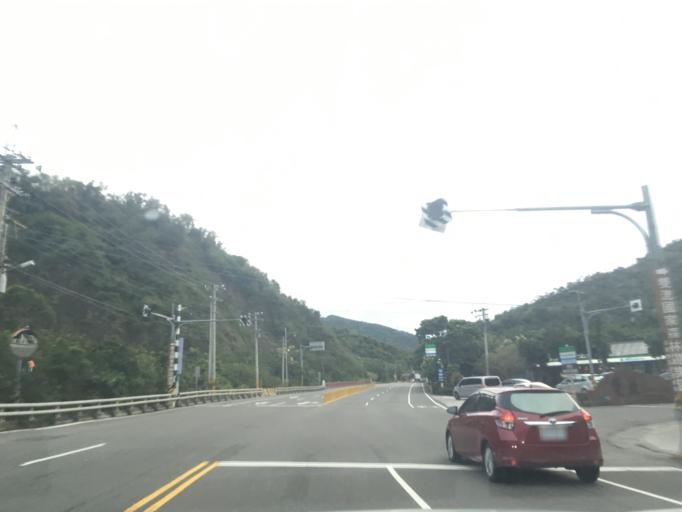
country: TW
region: Taiwan
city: Hengchun
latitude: 22.2184
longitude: 120.7936
